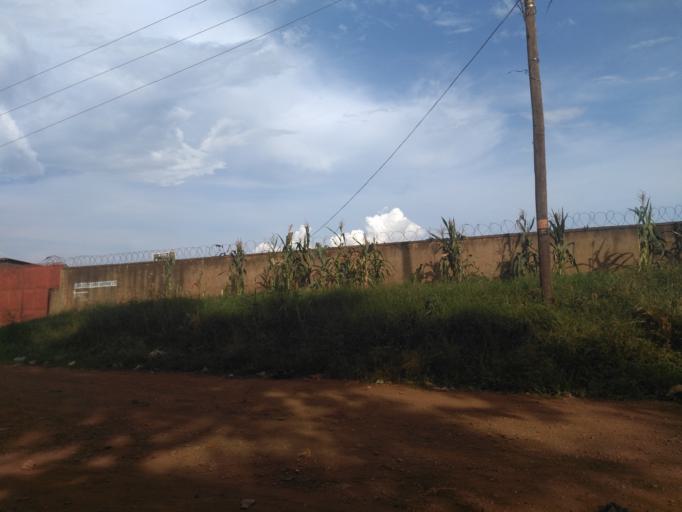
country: UG
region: Eastern Region
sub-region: Jinja District
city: Jinja
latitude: 0.4243
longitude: 33.2136
